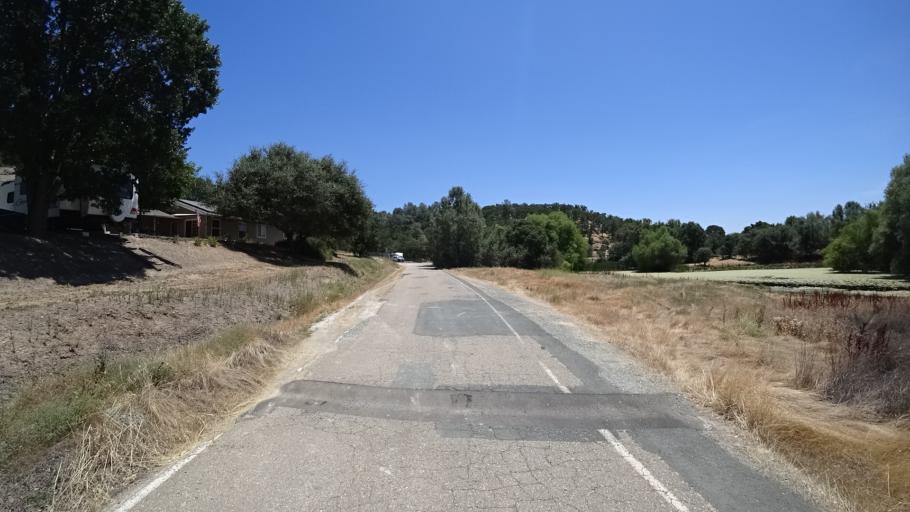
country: US
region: California
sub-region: Calaveras County
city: Rancho Calaveras
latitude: 38.1368
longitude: -120.8653
